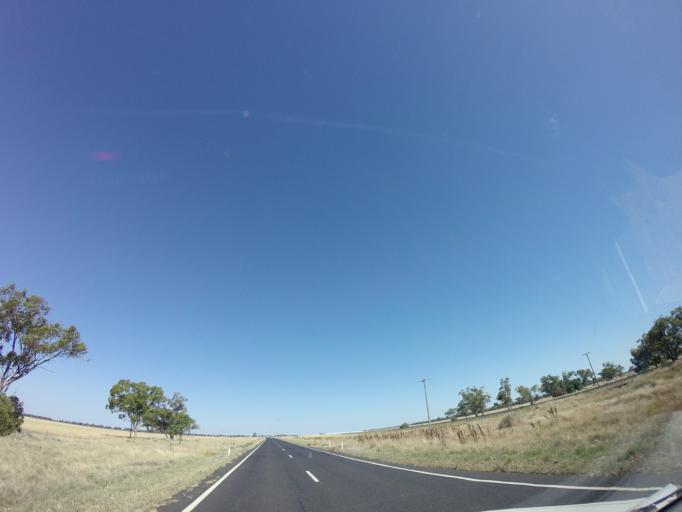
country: AU
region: New South Wales
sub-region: Bogan
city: Nyngan
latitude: -31.8265
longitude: 147.6961
